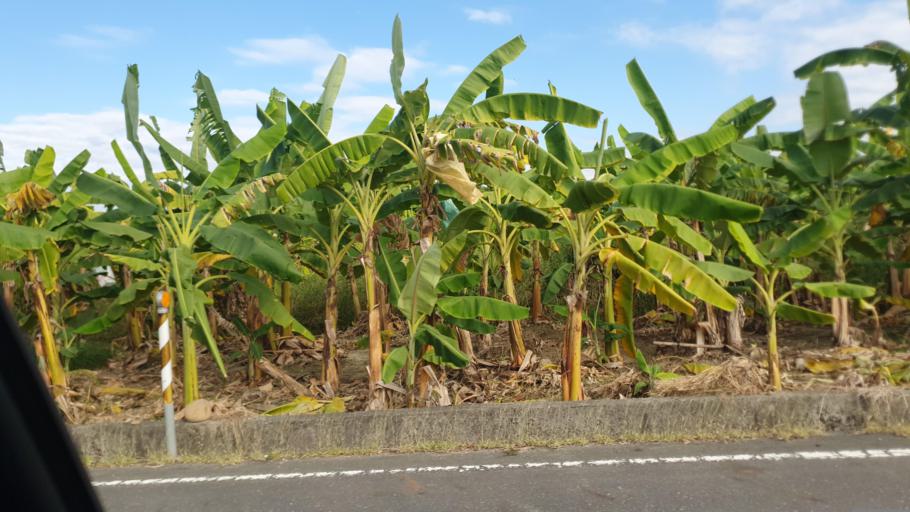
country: TW
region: Taiwan
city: Yujing
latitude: 23.0446
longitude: 120.4224
